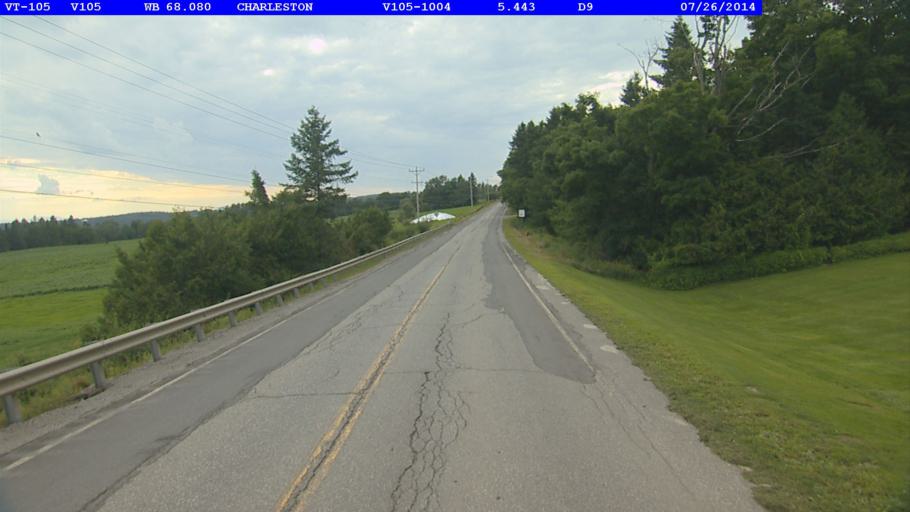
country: US
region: Vermont
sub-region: Orleans County
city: Newport
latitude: 44.8469
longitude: -72.0199
